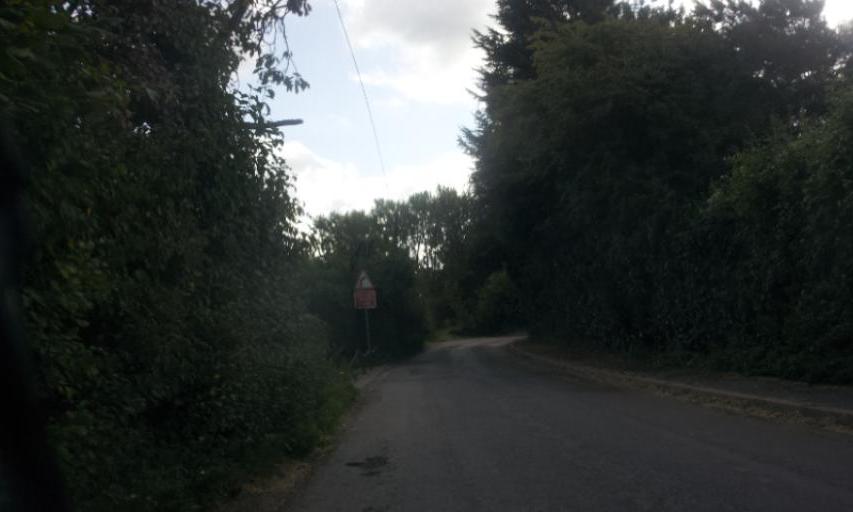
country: GB
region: England
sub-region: Kent
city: Sittingbourne
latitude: 51.3365
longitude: 0.6990
